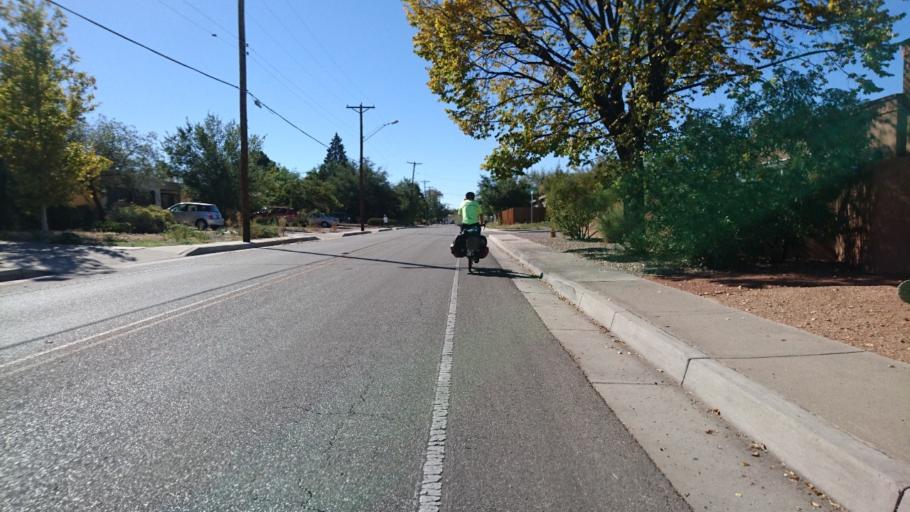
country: US
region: New Mexico
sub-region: Bernalillo County
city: Albuquerque
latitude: 35.0906
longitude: -106.5953
